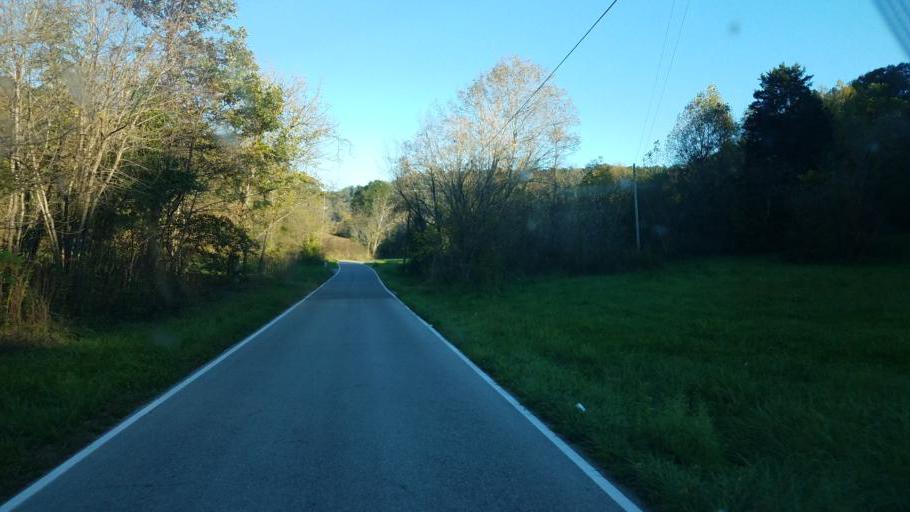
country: US
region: Ohio
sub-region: Adams County
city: Manchester
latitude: 38.5120
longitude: -83.5055
